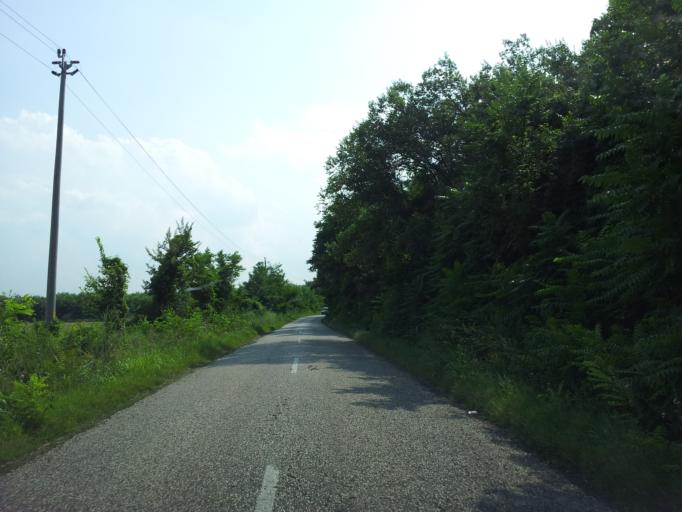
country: HU
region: Pest
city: Szigetujfalu
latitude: 47.2087
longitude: 18.9147
